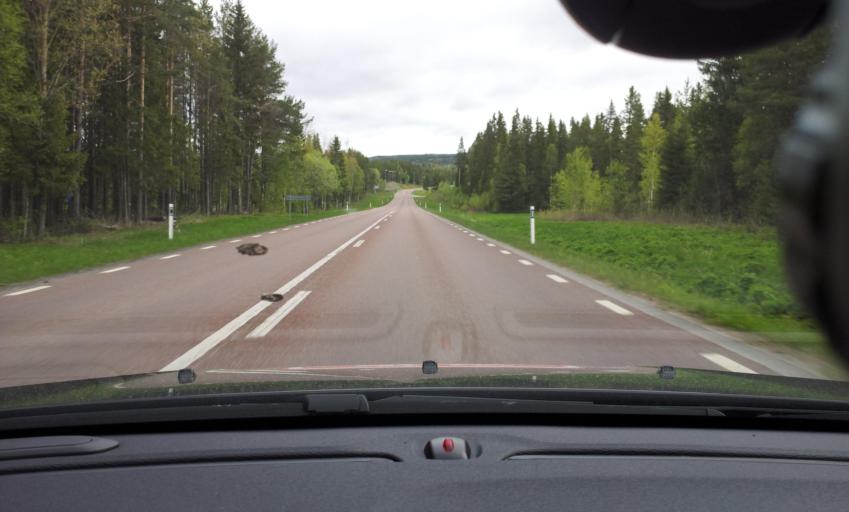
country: SE
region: Jaemtland
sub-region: OEstersunds Kommun
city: Brunflo
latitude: 63.0596
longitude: 14.8342
